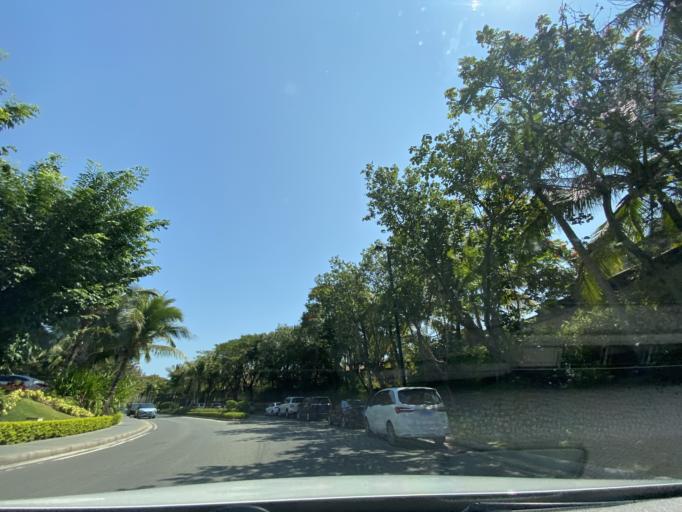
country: CN
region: Hainan
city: Yingzhou
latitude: 18.4041
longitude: 109.8464
